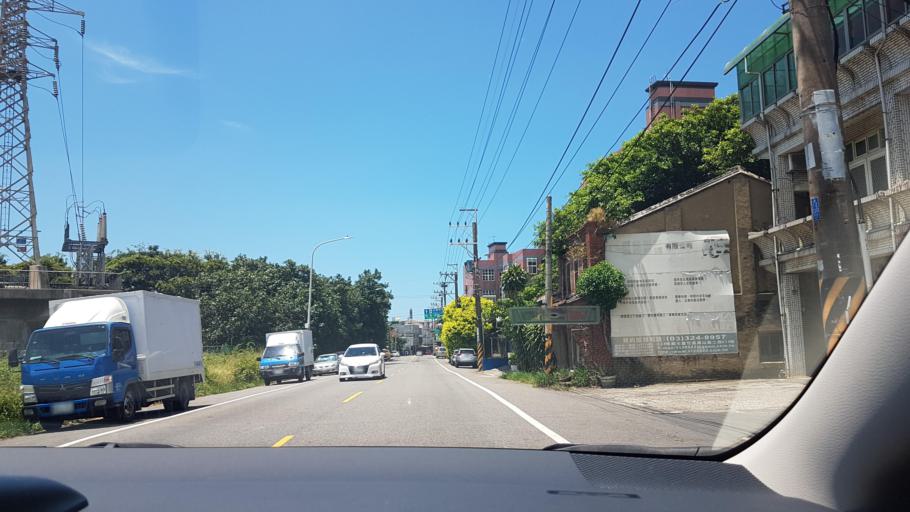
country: TW
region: Taiwan
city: Taoyuan City
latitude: 25.0994
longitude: 121.2622
